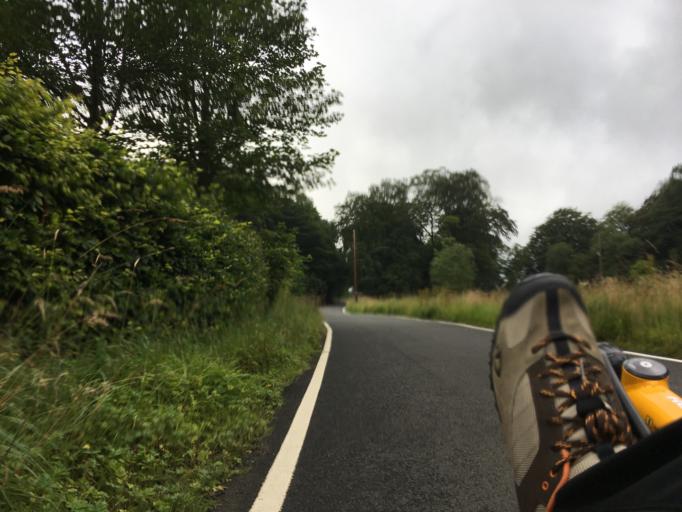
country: GB
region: Scotland
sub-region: West Lothian
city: West Calder
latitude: 55.8396
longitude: -3.5288
